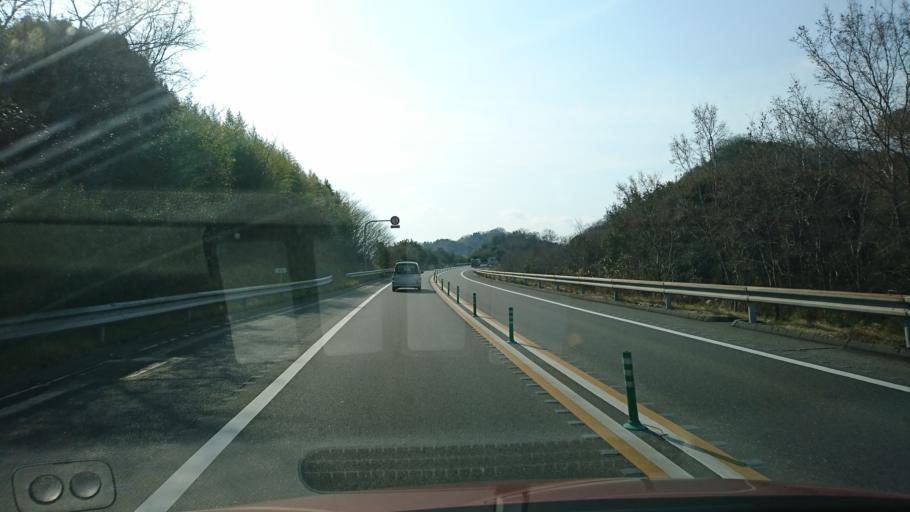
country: JP
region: Hiroshima
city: Onomichi
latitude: 34.3913
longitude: 133.2060
